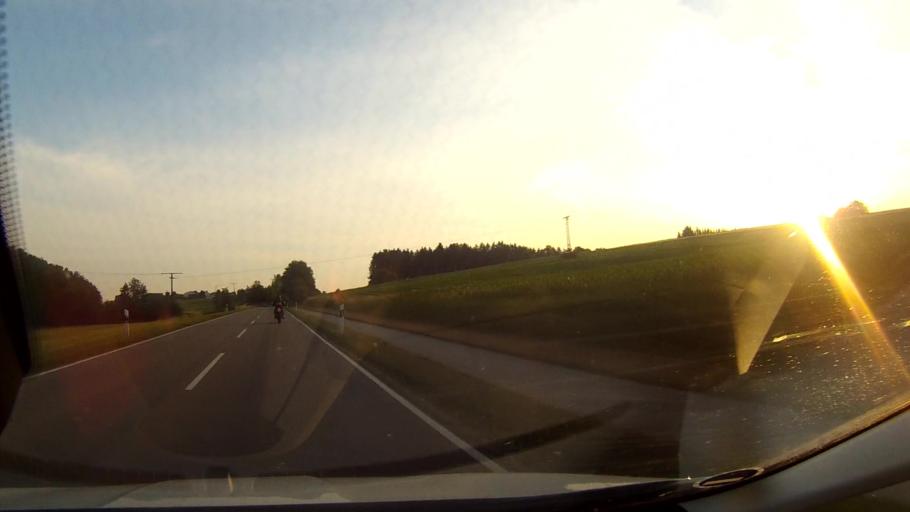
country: DE
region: Baden-Wuerttemberg
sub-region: Tuebingen Region
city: Staig
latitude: 48.2973
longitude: 9.9849
